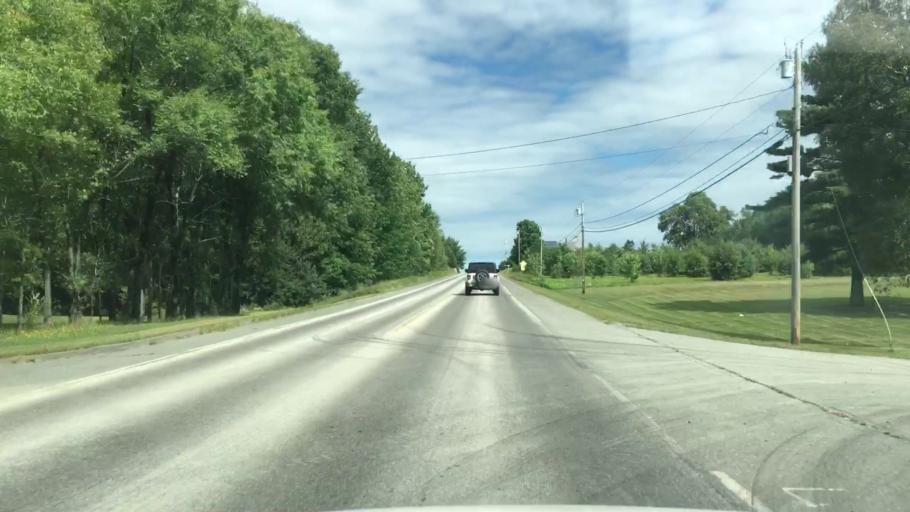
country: US
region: Maine
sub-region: Piscataquis County
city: Dover-Foxcroft
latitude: 45.1607
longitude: -69.2322
